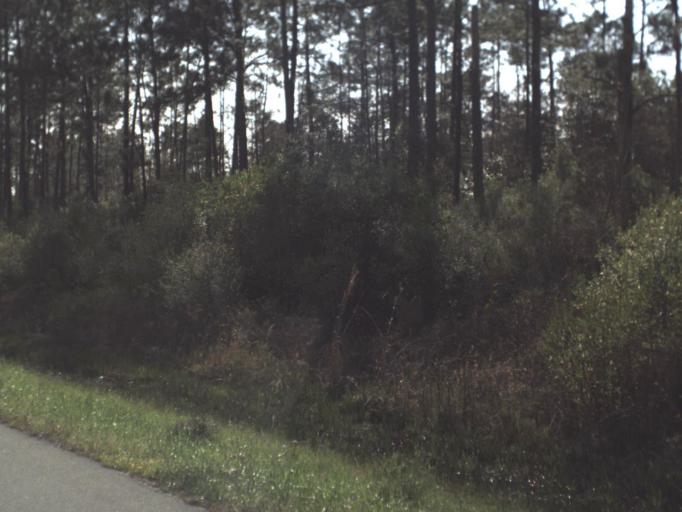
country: US
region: Florida
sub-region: Wakulla County
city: Crawfordville
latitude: 30.0285
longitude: -84.4983
